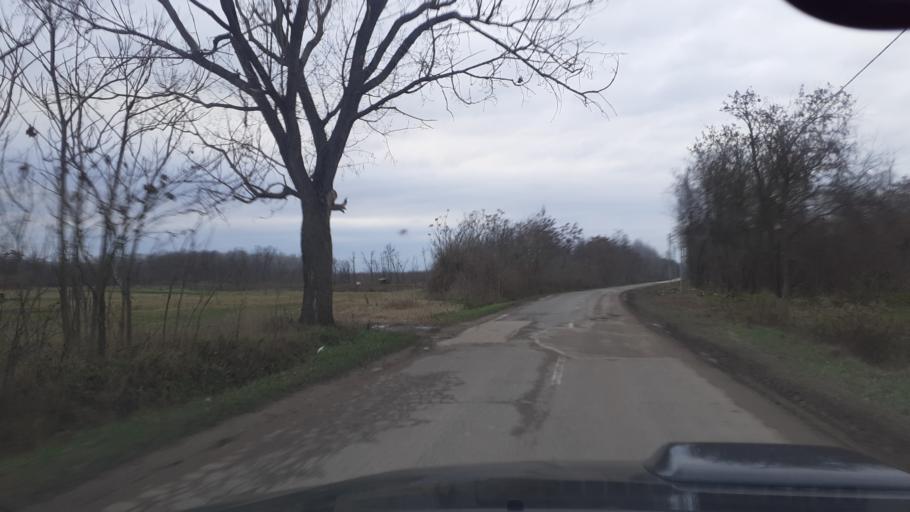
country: HU
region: Bacs-Kiskun
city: Szalkszentmarton
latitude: 46.9479
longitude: 19.0676
